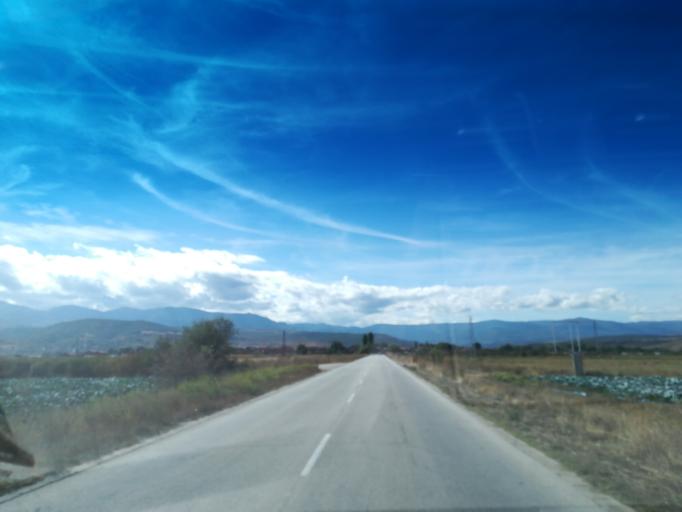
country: BG
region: Plovdiv
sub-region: Obshtina Krichim
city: Krichim
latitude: 42.0893
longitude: 24.4429
